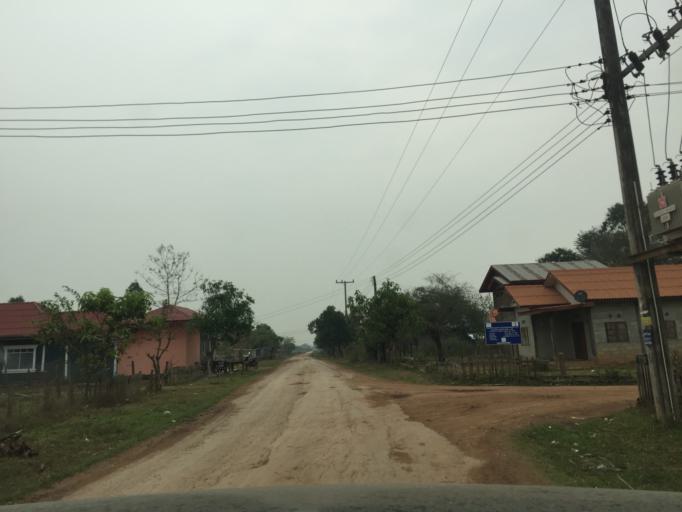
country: LA
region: Xiagnabouli
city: Sainyabuli
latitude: 19.0875
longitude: 101.5348
